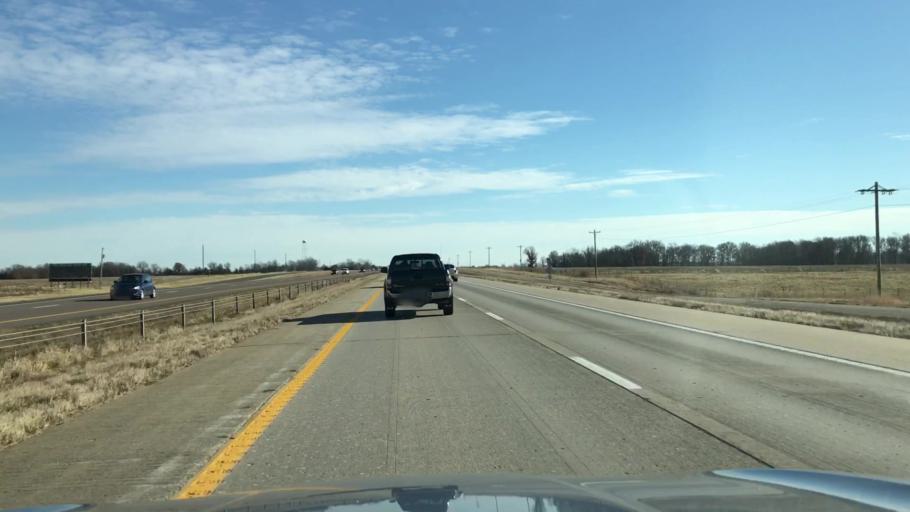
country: US
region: Missouri
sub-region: Callaway County
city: Fulton
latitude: 38.9214
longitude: -91.7604
